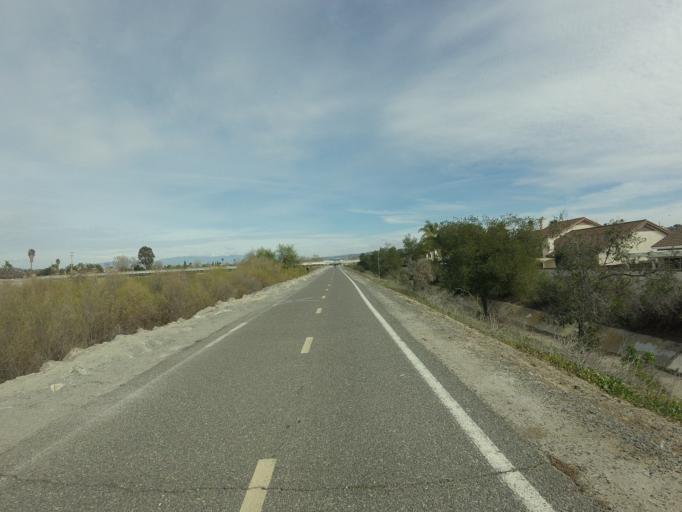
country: US
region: California
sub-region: San Diego County
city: Camp Pendleton South
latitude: 33.2397
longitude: -117.3247
